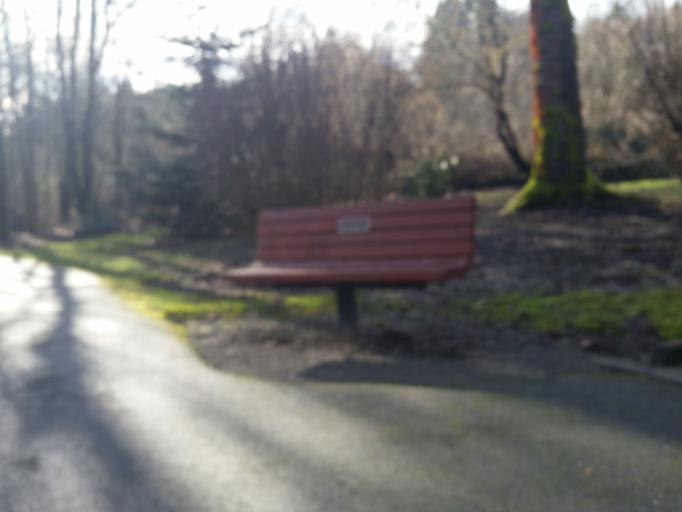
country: US
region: Washington
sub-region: King County
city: Bothell
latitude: 47.7574
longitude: -122.2100
